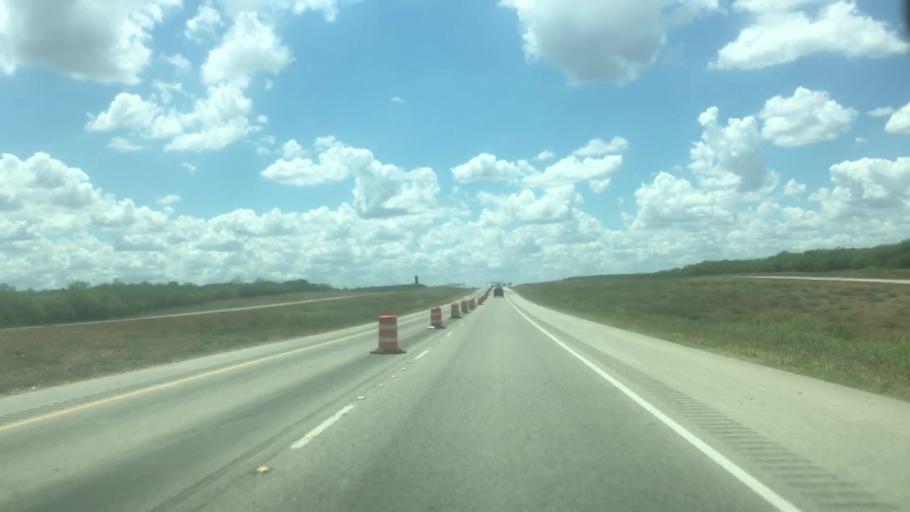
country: US
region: Texas
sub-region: Caldwell County
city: Martindale
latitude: 29.8220
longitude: -97.7529
